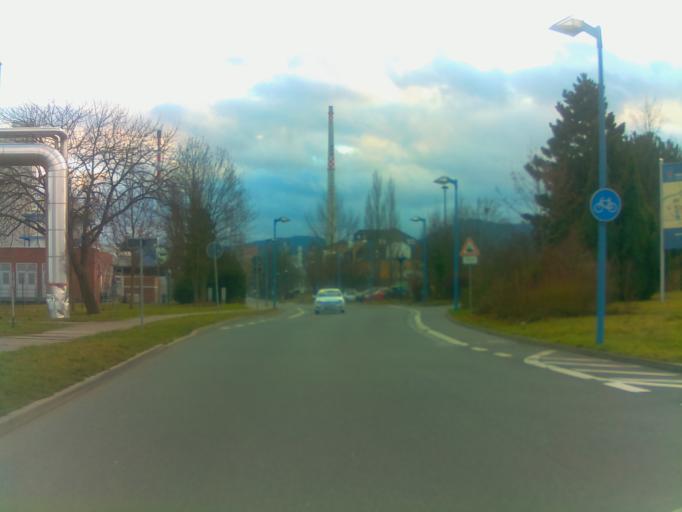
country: DE
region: Thuringia
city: Rudolstadt
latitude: 50.6941
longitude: 11.3296
